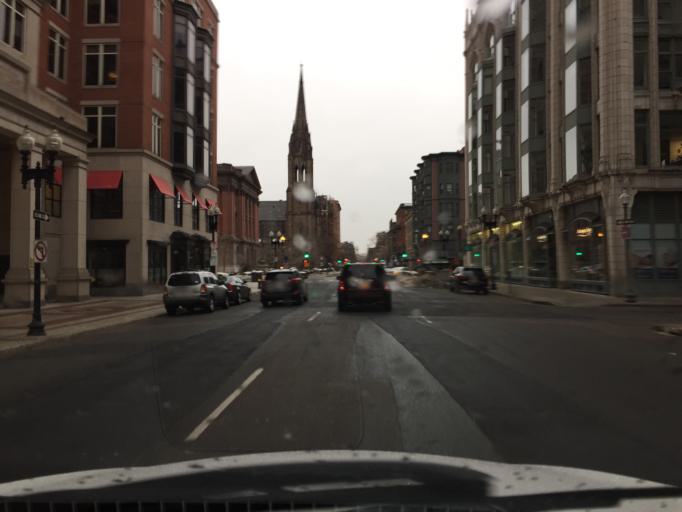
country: US
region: Massachusetts
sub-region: Suffolk County
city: Boston
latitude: 42.3505
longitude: -71.0727
